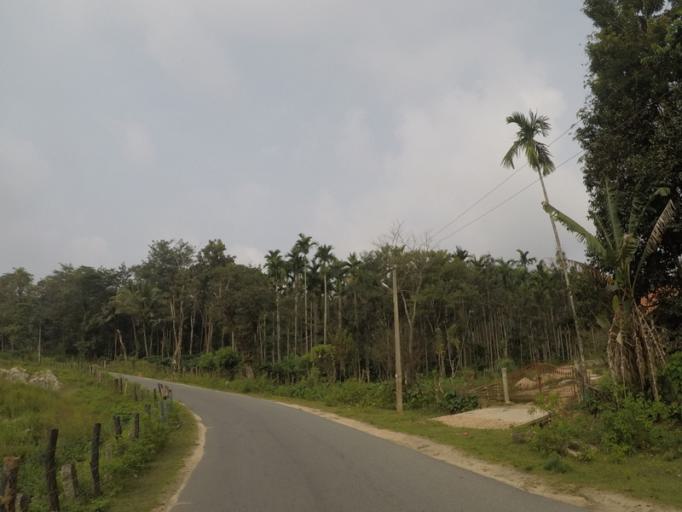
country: IN
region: Karnataka
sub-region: Chikmagalur
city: Koppa
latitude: 13.3634
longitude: 75.5088
